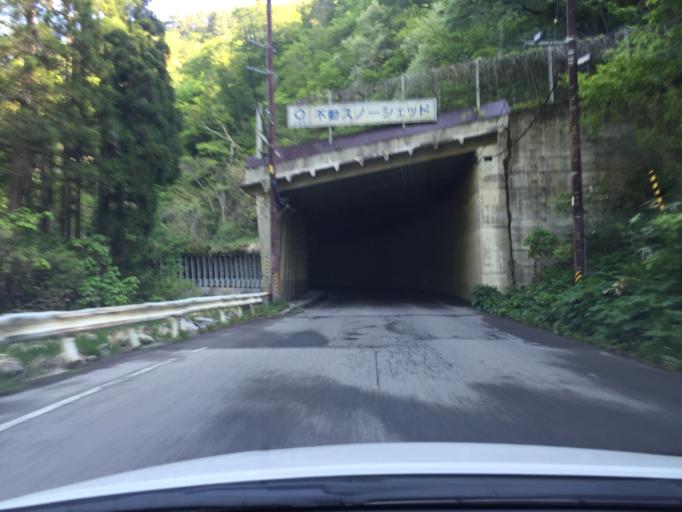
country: JP
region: Fukushima
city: Kitakata
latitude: 37.6772
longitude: 139.7240
